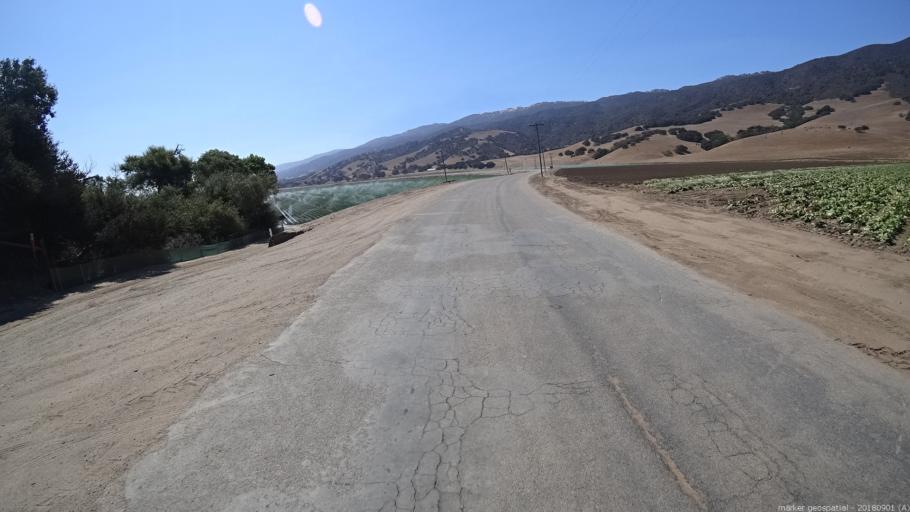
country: US
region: California
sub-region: Monterey County
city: Chualar
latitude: 36.5399
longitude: -121.5412
